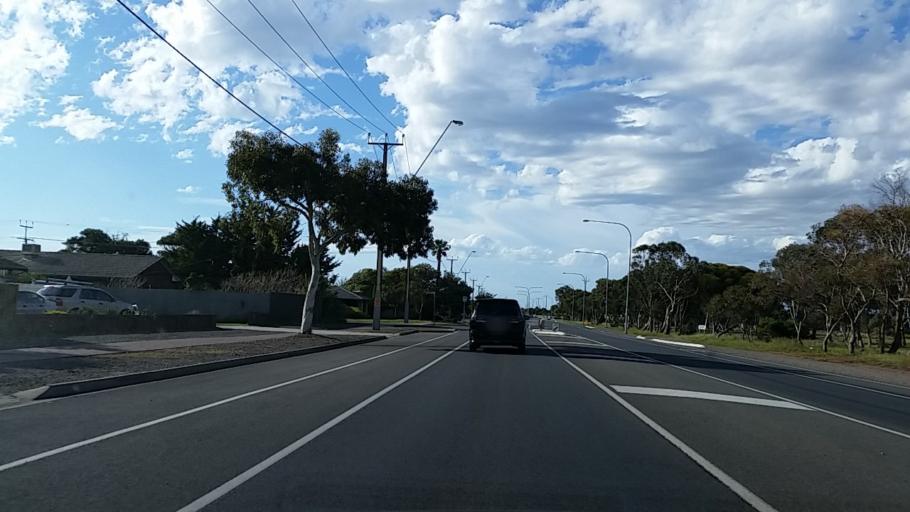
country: AU
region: South Australia
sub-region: Onkaparinga
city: Seaford
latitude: -35.1846
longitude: 138.4770
